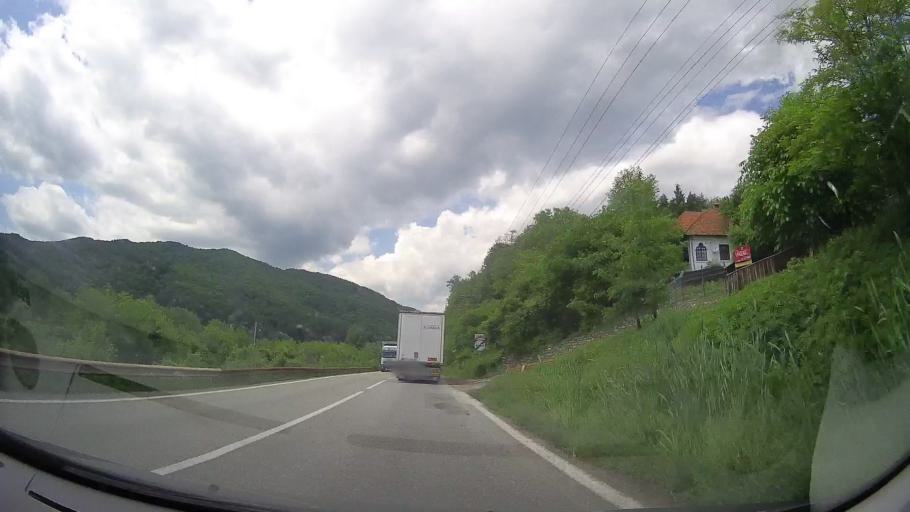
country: RO
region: Valcea
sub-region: Oras Calimanesti
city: Jiblea Veche
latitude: 45.2470
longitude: 24.3453
